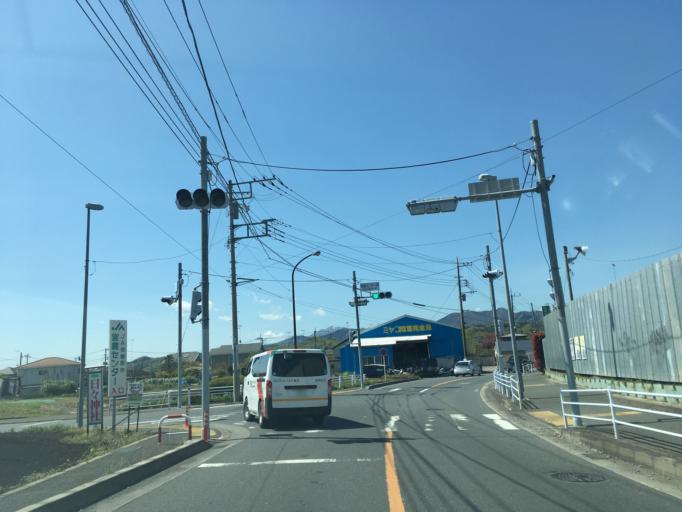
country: JP
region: Tokyo
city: Hachioji
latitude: 35.5719
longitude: 139.3235
